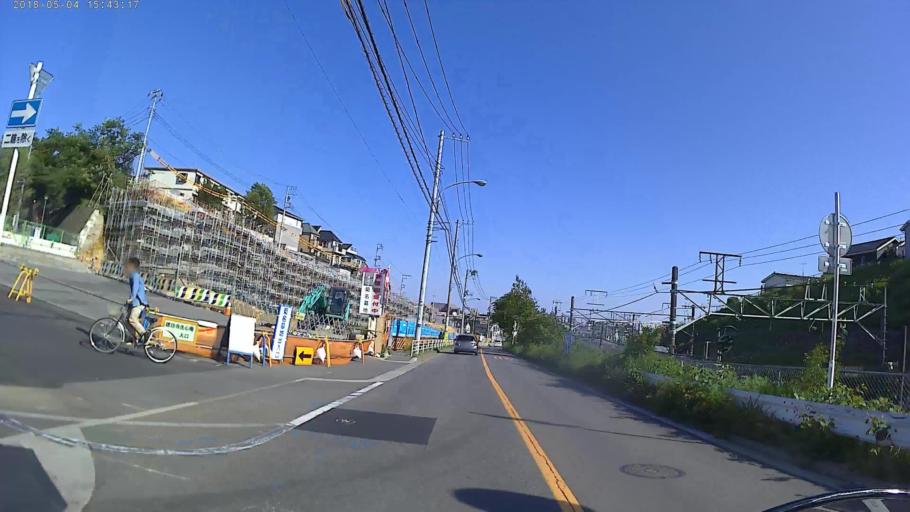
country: JP
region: Kanagawa
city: Yokohama
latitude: 35.5054
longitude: 139.6411
